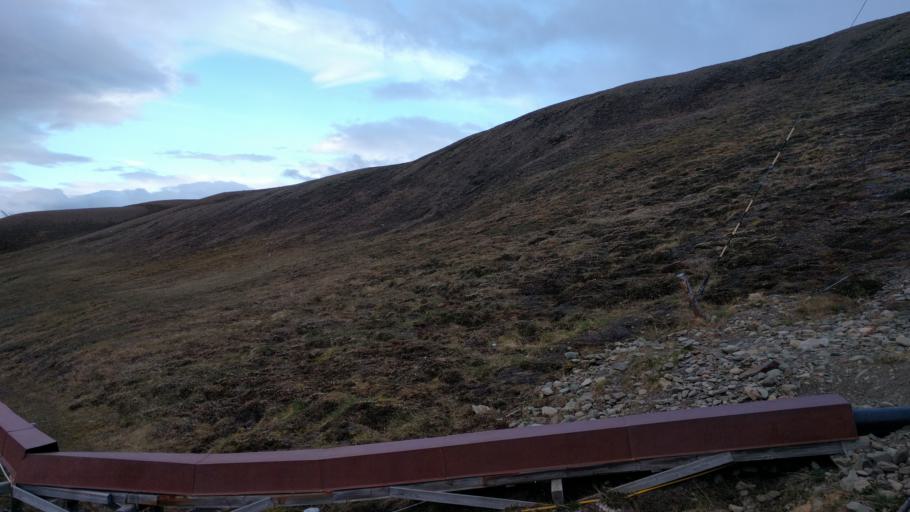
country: SJ
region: Svalbard
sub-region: Spitsbergen
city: Longyearbyen
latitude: 78.2182
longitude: 15.6770
